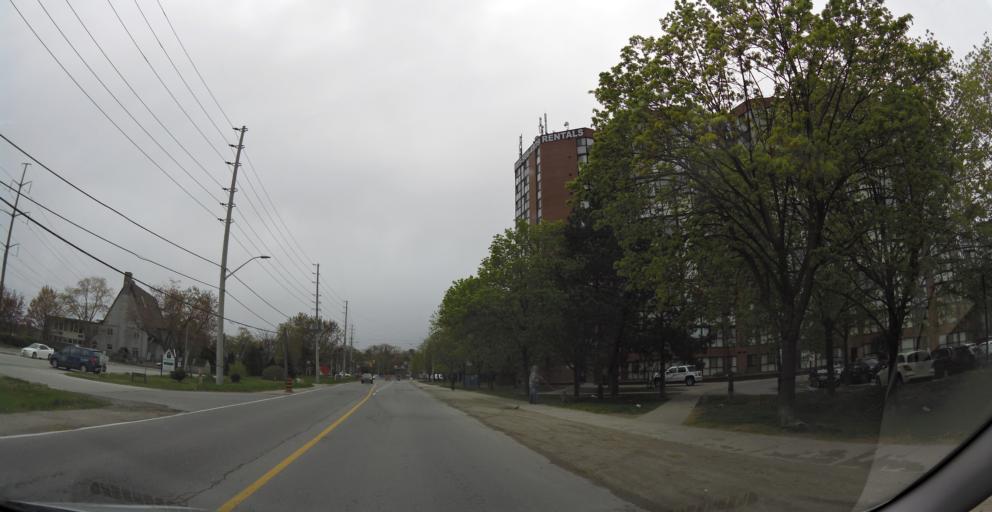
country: CA
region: Ontario
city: Mississauga
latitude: 43.5711
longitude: -79.5997
